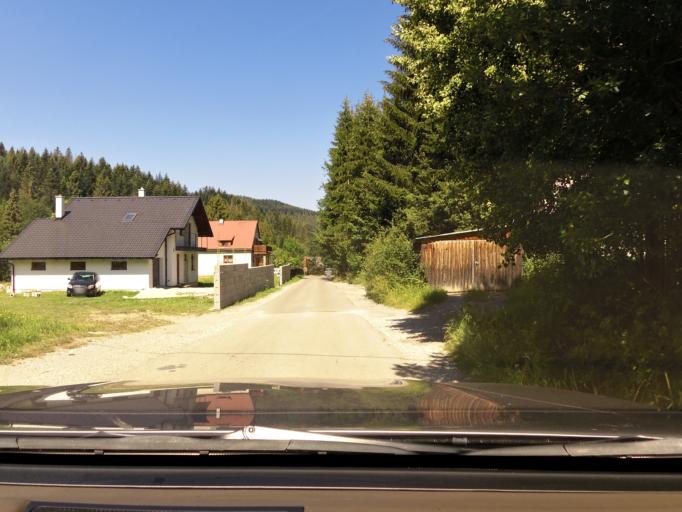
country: PL
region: Silesian Voivodeship
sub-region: Powiat cieszynski
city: Koniakow
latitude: 49.4720
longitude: 18.9227
